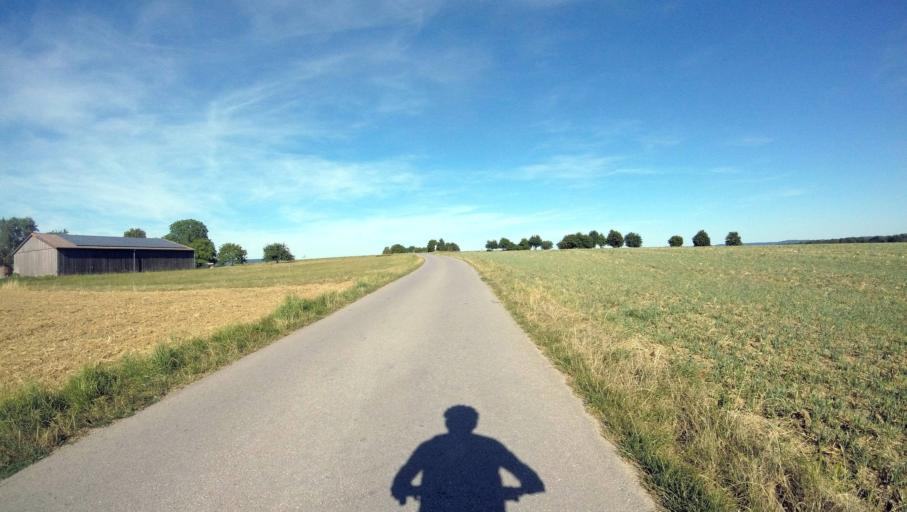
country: DE
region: Baden-Wuerttemberg
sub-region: Regierungsbezirk Stuttgart
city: Kirchberg an der Murr
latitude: 48.9545
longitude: 9.3509
